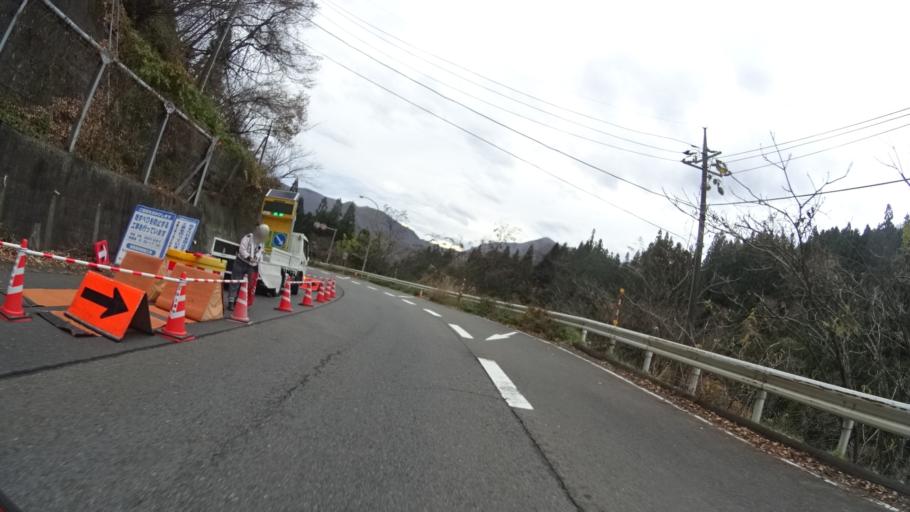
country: JP
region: Gunma
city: Nakanojomachi
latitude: 36.7334
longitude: 138.8520
